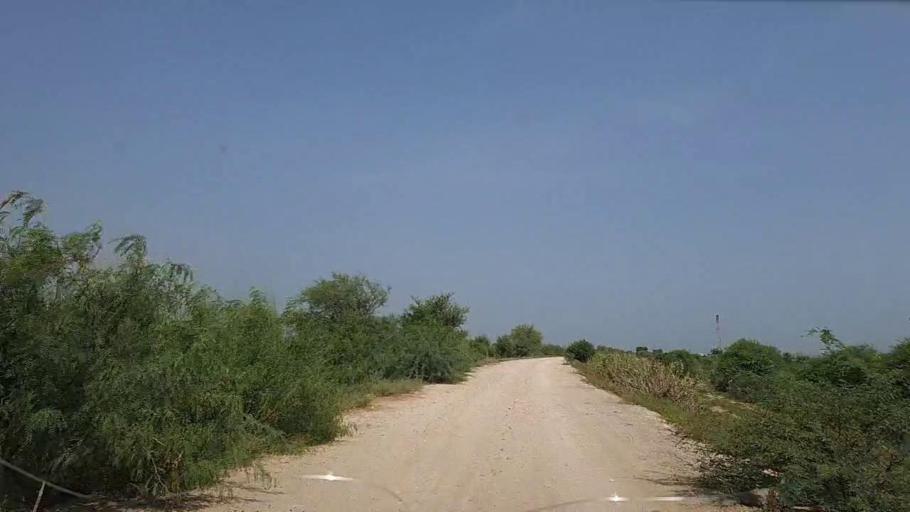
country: PK
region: Sindh
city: Ghotki
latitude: 28.1188
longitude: 69.3785
